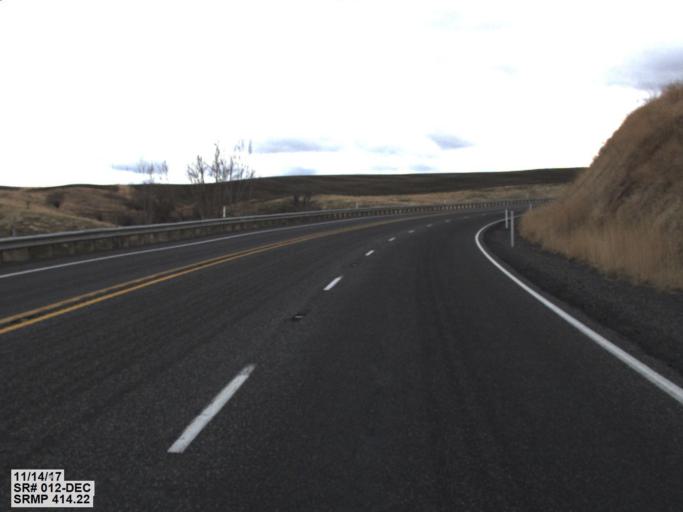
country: US
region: Washington
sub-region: Garfield County
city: Pomeroy
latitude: 46.4401
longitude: -117.4078
